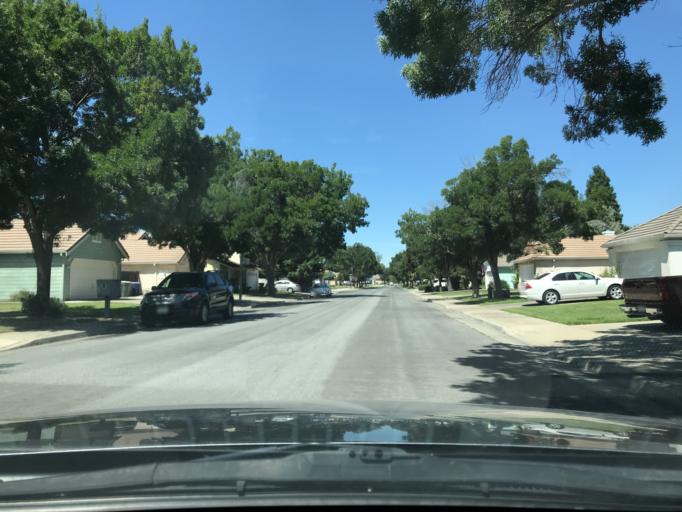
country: US
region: California
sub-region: Merced County
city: Merced
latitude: 37.3276
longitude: -120.4719
